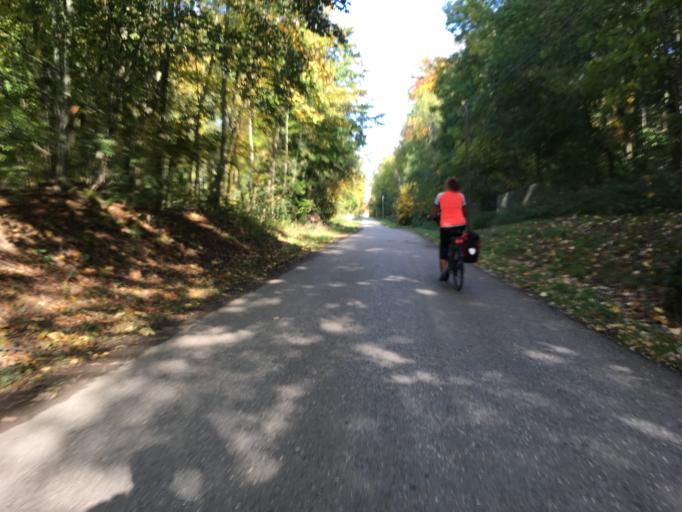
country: DE
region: Baden-Wuerttemberg
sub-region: Regierungsbezirk Stuttgart
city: Siegelsbach
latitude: 49.2648
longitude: 9.0426
